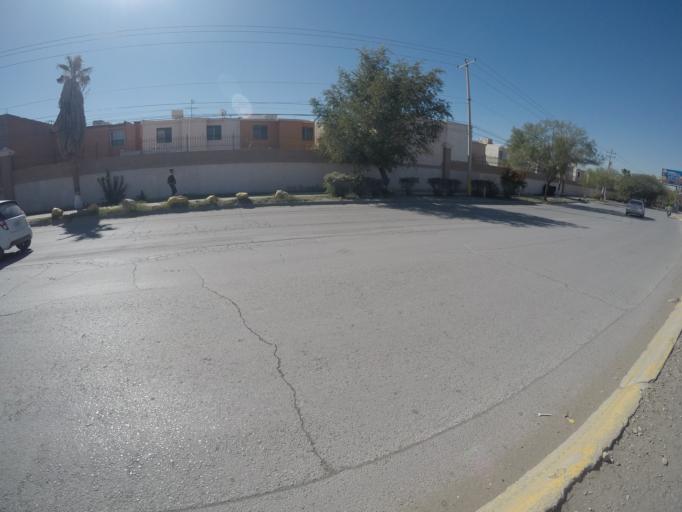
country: US
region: Texas
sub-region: El Paso County
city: Socorro
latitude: 31.6944
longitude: -106.3755
